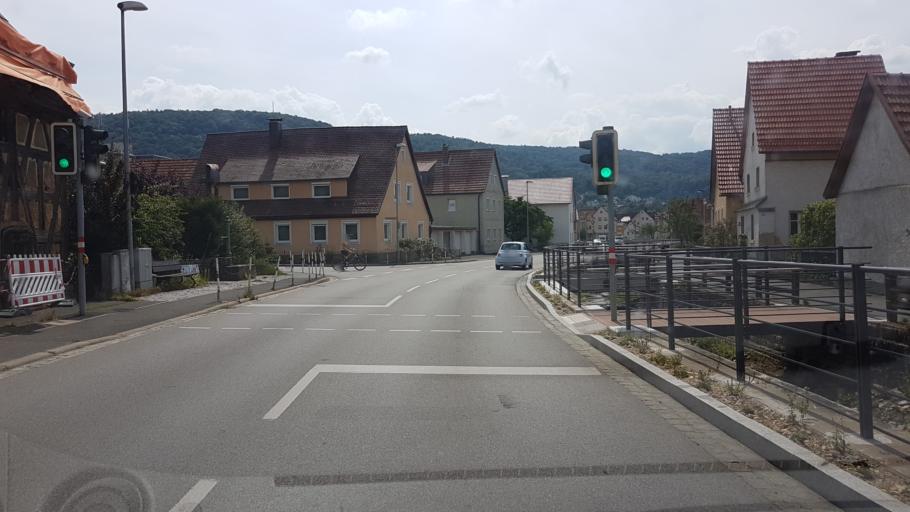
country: DE
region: Bavaria
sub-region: Upper Franconia
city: Ebermannstadt
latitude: 49.7835
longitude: 11.1835
